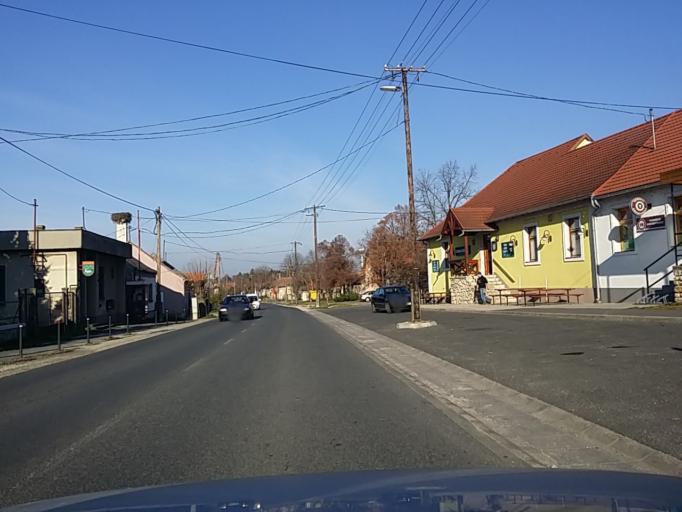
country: HU
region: Veszprem
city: Tapolca
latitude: 46.8674
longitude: 17.4811
